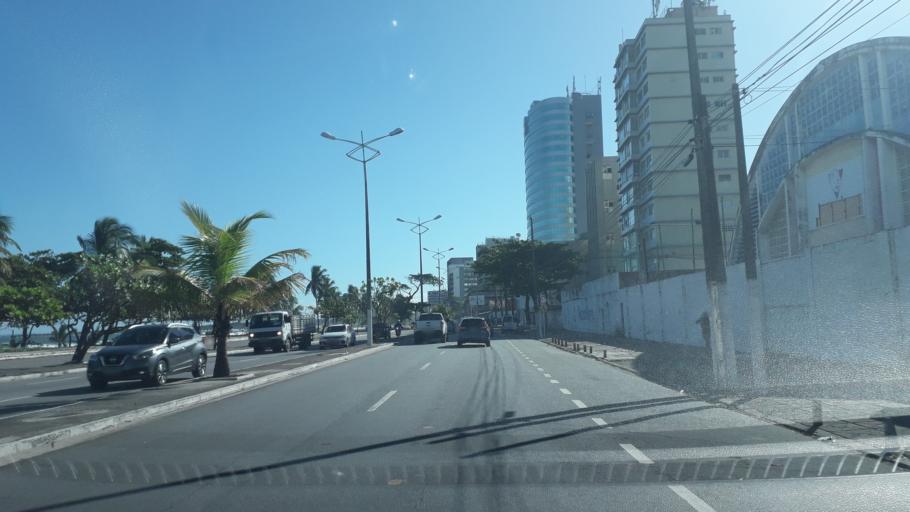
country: BR
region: Alagoas
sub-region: Maceio
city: Maceio
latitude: -9.6696
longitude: -35.7341
